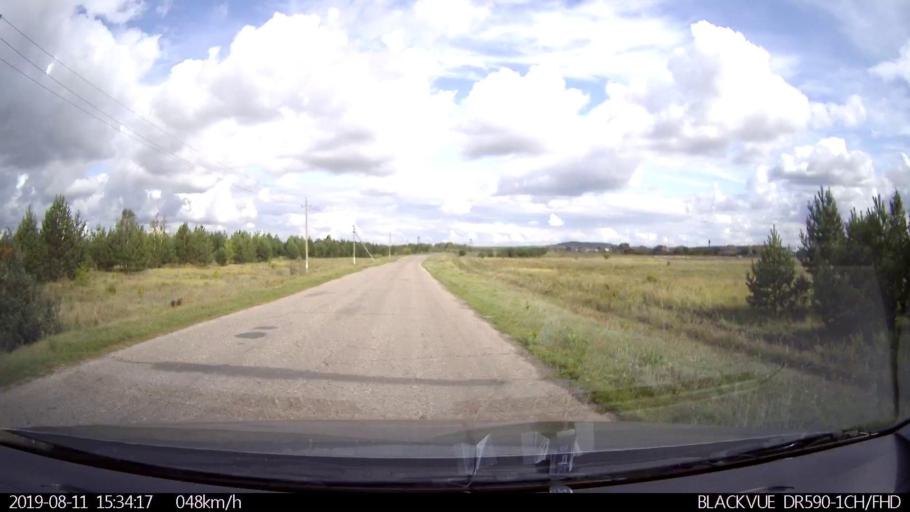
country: RU
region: Ulyanovsk
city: Ignatovka
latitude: 53.8618
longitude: 47.5935
